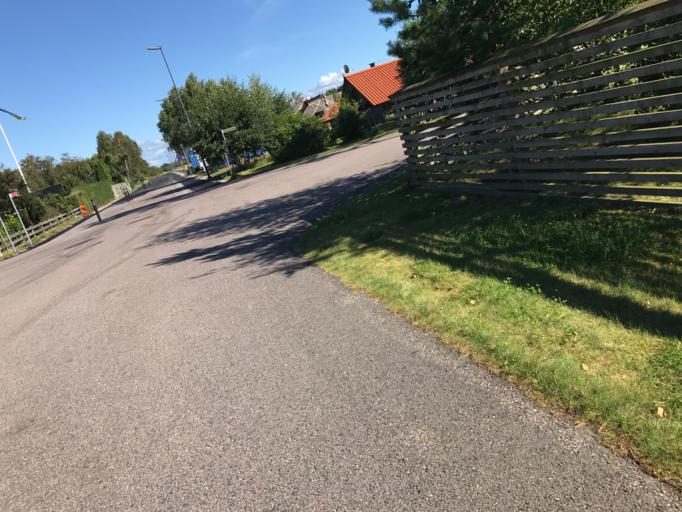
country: SE
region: Skane
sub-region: Bastads Kommun
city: Bastad
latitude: 56.4462
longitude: 12.9047
